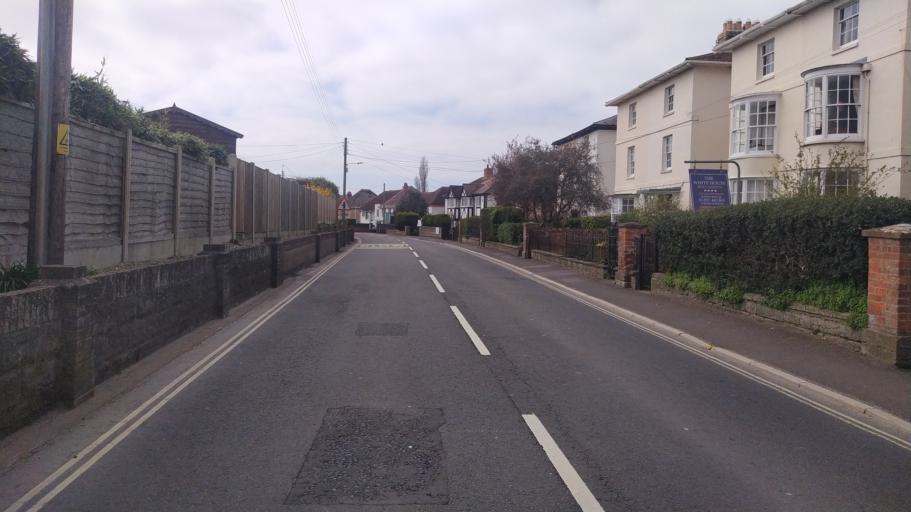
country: GB
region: England
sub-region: Dorset
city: Bridport
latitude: 50.7221
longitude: -2.7578
